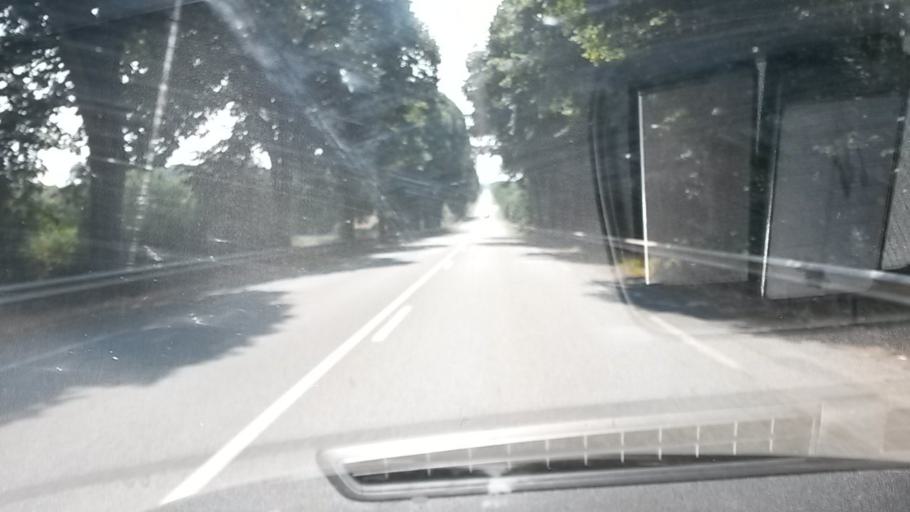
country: FR
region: Pays de la Loire
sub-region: Departement de la Mayenne
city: Chateau-Gontier
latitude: 47.8670
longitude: -0.6888
